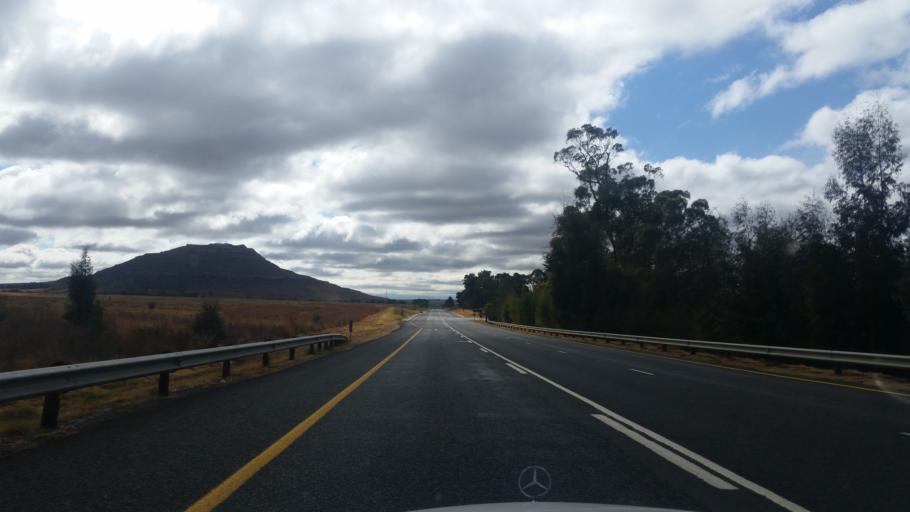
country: ZA
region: Orange Free State
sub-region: Thabo Mofutsanyana District Municipality
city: Phuthaditjhaba
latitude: -28.3133
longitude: 28.7261
